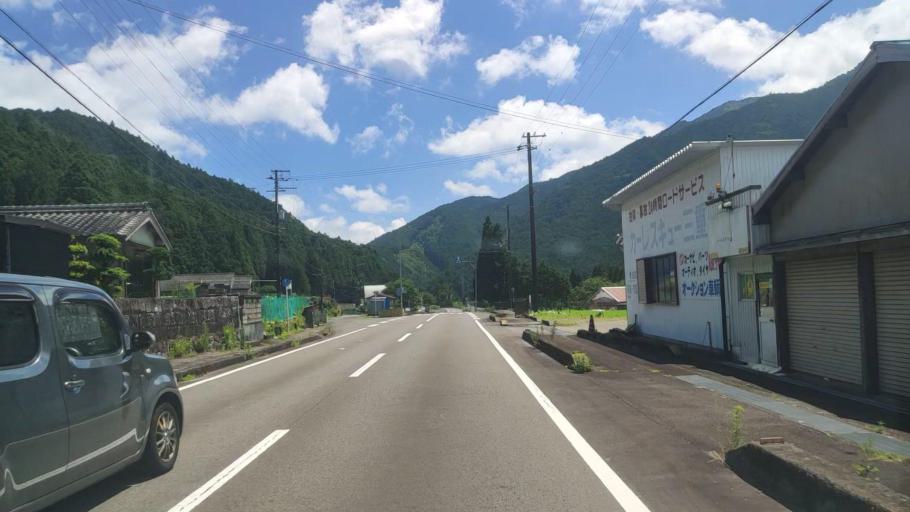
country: JP
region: Mie
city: Owase
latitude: 33.9785
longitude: 136.1046
